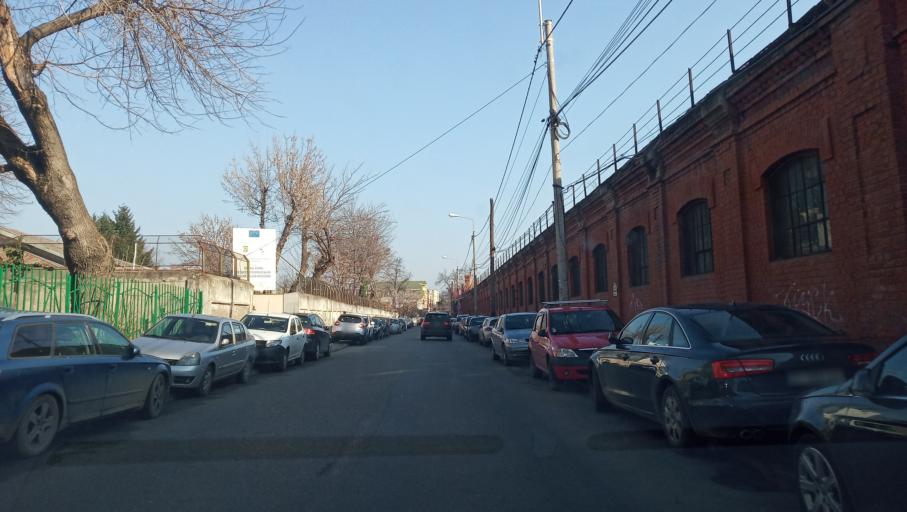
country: RO
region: Bucuresti
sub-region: Municipiul Bucuresti
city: Bucharest
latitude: 44.4544
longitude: 26.1154
